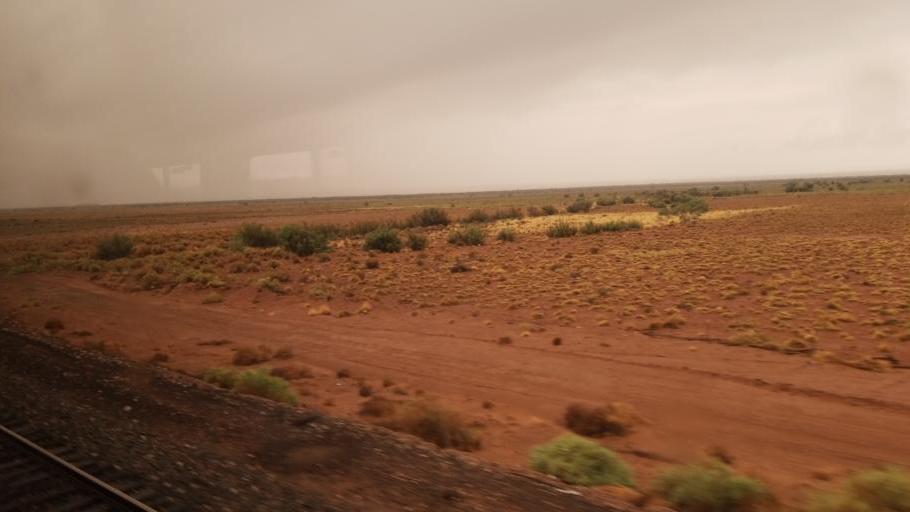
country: US
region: Arizona
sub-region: Navajo County
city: Joseph City
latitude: 34.9675
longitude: -110.5057
